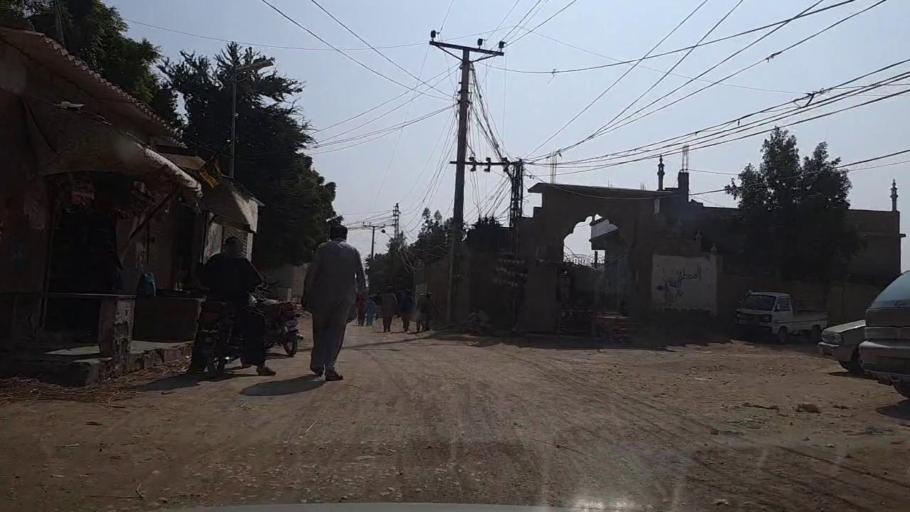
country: PK
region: Sindh
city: Mirpur Sakro
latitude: 24.5492
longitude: 67.6265
